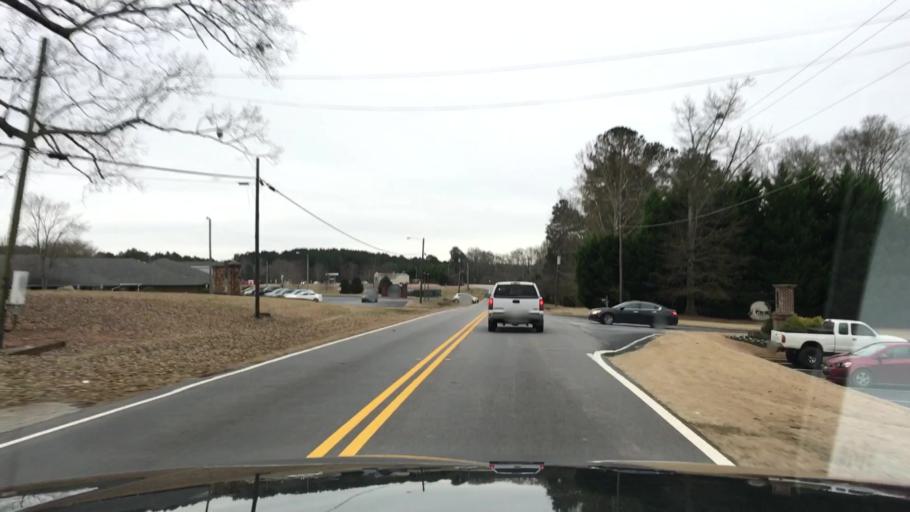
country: US
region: Georgia
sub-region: Walton County
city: Monroe
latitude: 33.8364
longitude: -83.7348
